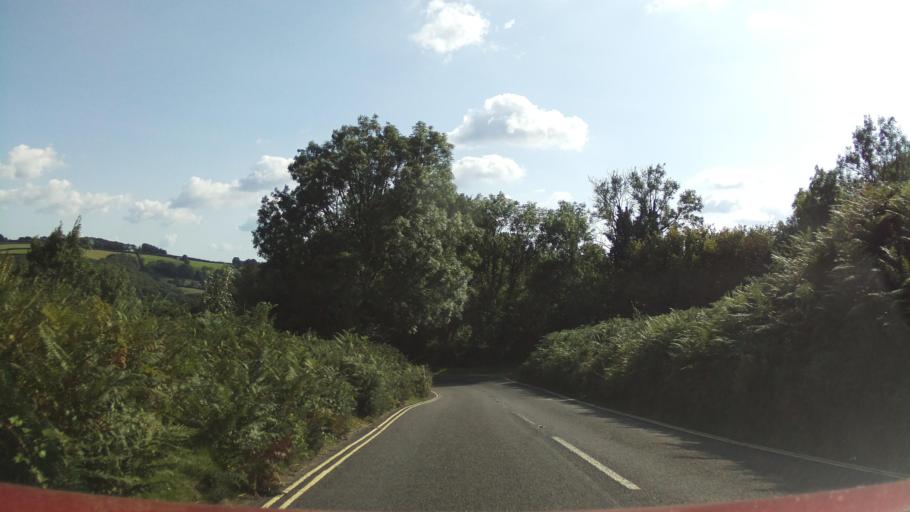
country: GB
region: England
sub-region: Devon
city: Buckfastleigh
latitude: 50.5270
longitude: -3.8238
